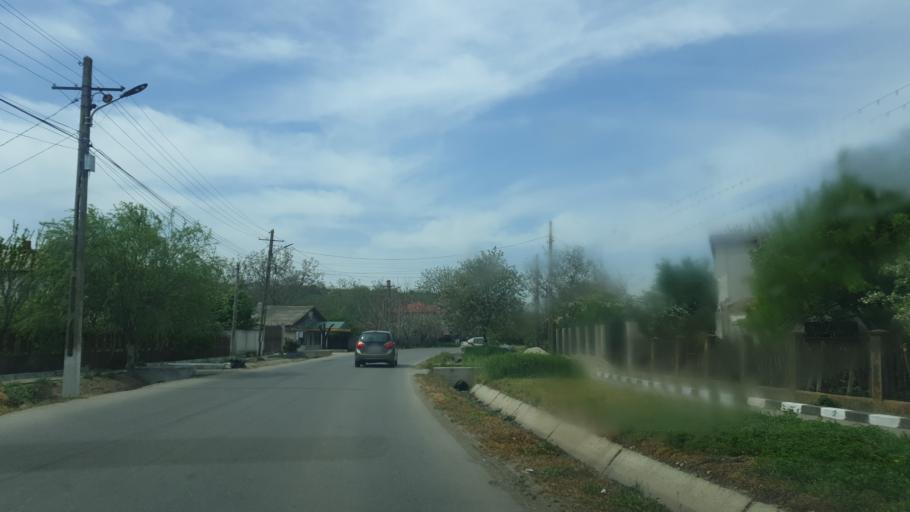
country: RO
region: Giurgiu
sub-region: Comuna Hotarele
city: Hotarele
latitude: 44.1770
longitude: 26.3796
